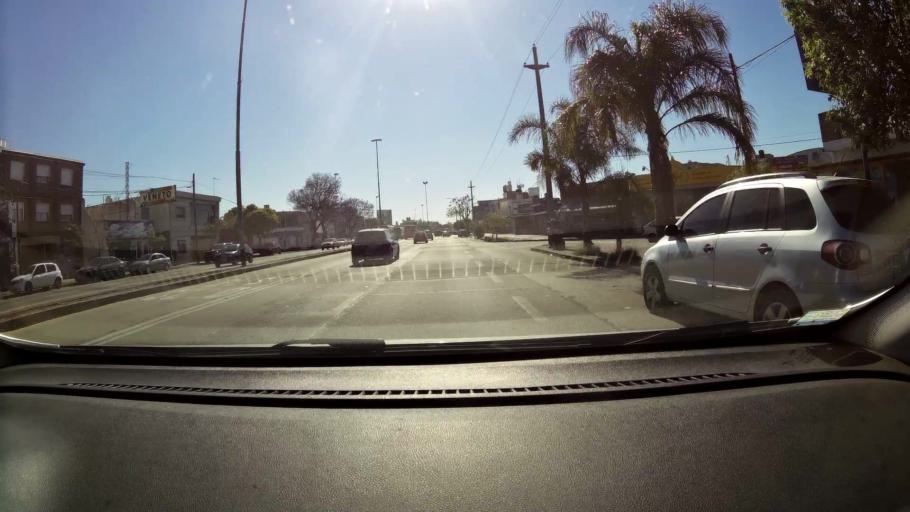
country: AR
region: Cordoba
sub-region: Departamento de Capital
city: Cordoba
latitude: -31.4332
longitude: -64.1537
